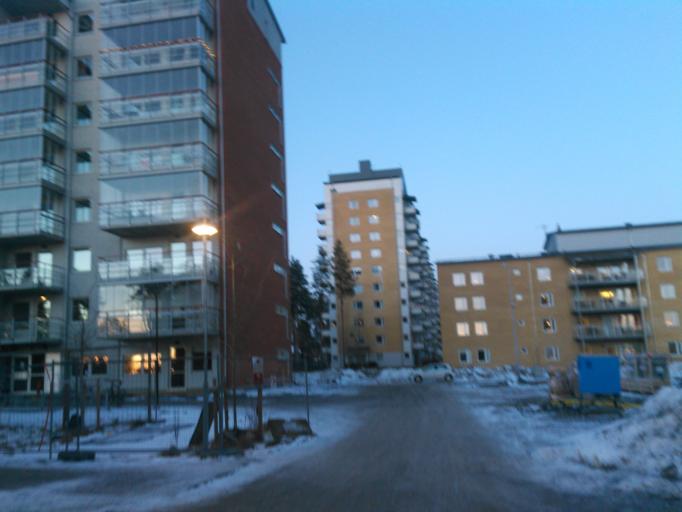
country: SE
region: Vaesterbotten
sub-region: Umea Kommun
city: Ersmark
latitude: 63.8301
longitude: 20.3258
